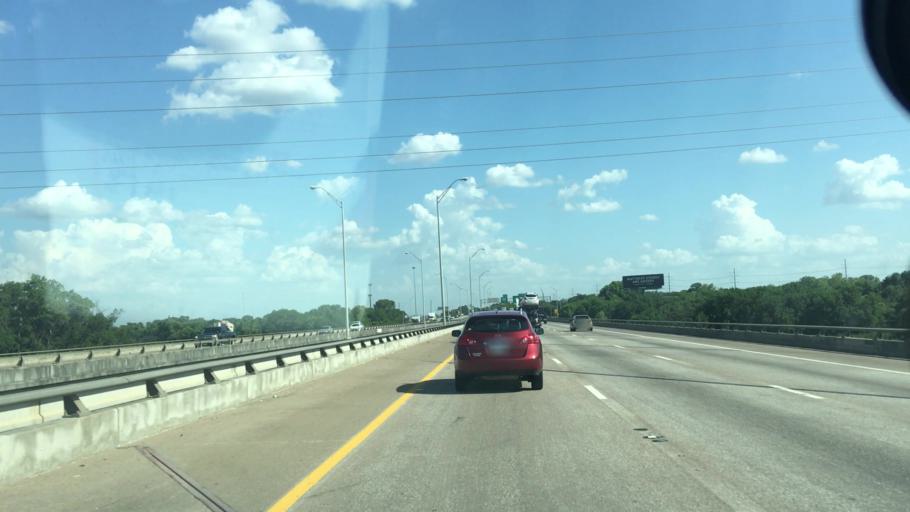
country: US
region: Texas
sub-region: Dallas County
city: Dallas
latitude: 32.7303
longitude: -96.7641
